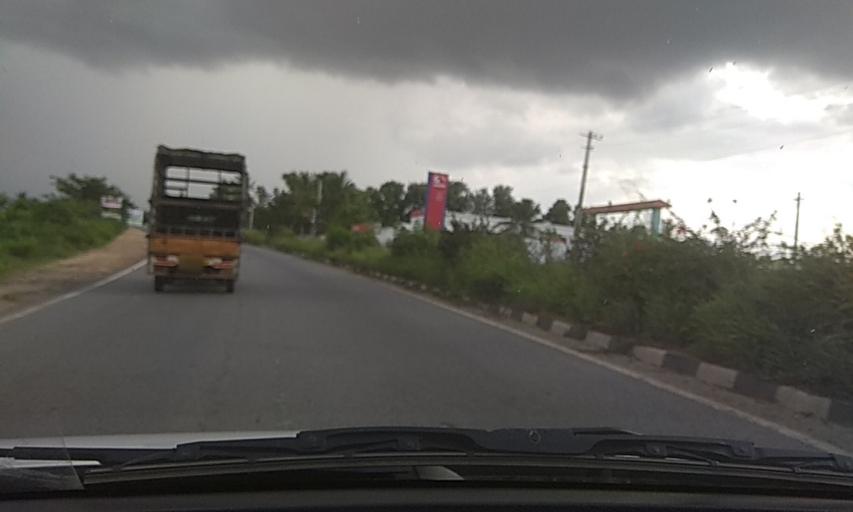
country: IN
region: Karnataka
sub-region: Mandya
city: Shrirangapattana
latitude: 12.3912
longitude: 76.6670
